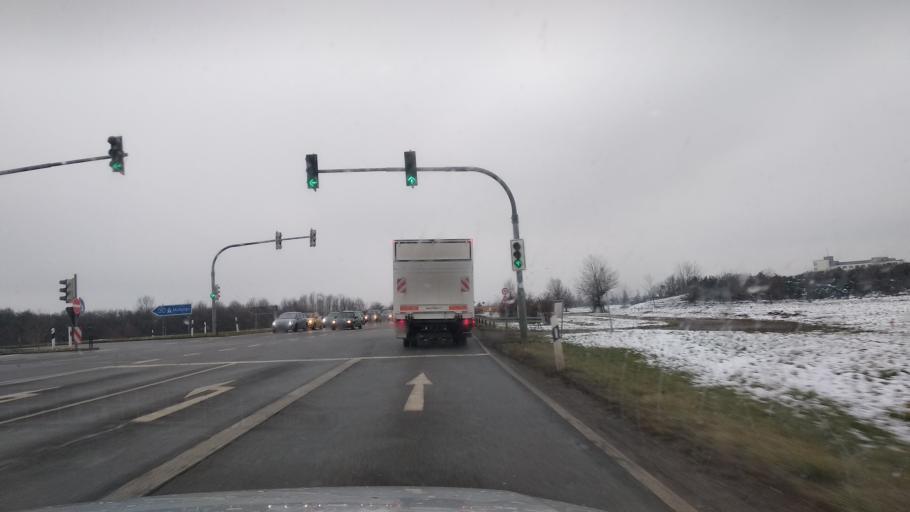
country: DE
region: Bavaria
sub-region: Upper Bavaria
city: Feldkirchen
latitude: 48.1448
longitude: 11.7454
